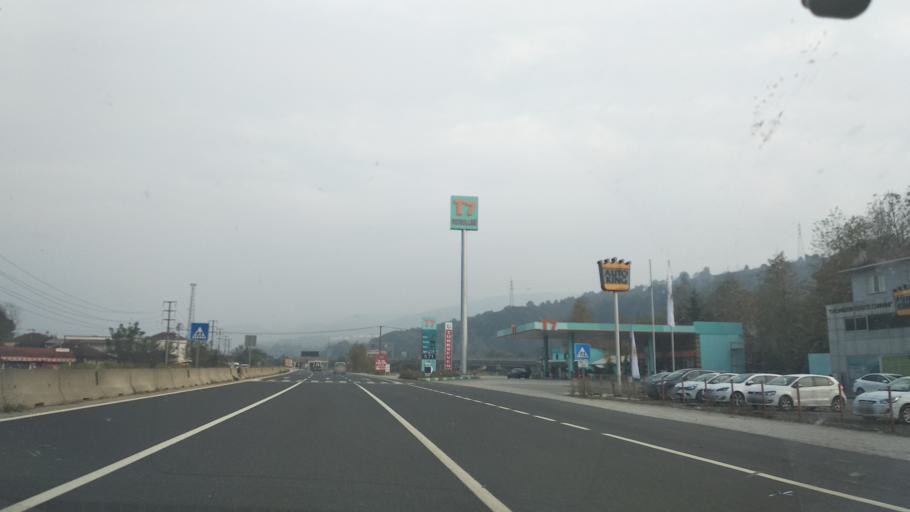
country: TR
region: Duzce
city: Kaynasli
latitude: 40.7883
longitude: 31.2611
